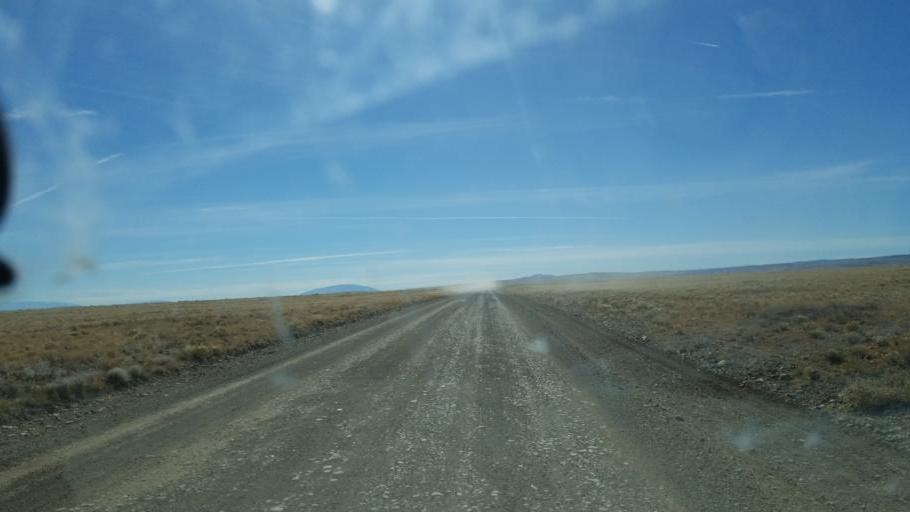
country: US
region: Colorado
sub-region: Rio Grande County
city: Monte Vista
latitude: 37.3462
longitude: -106.1491
